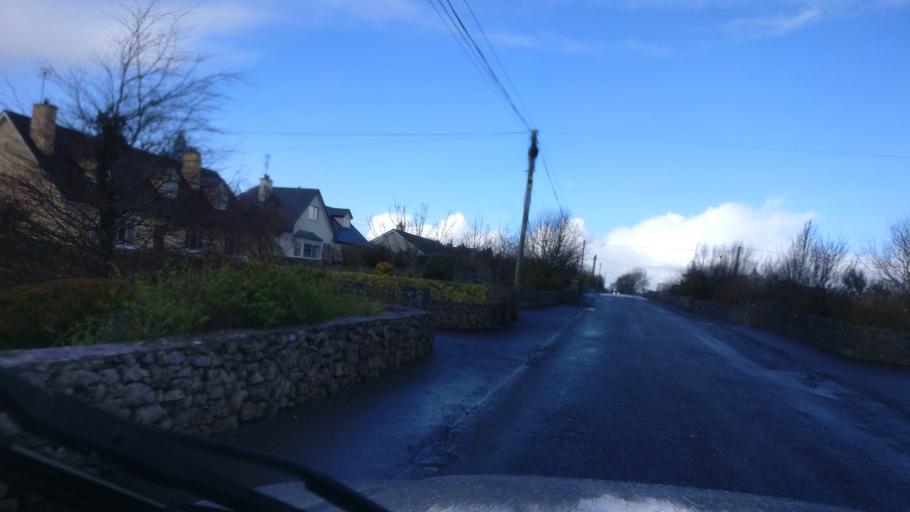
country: IE
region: Connaught
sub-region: County Galway
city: Oranmore
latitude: 53.2566
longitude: -8.8557
